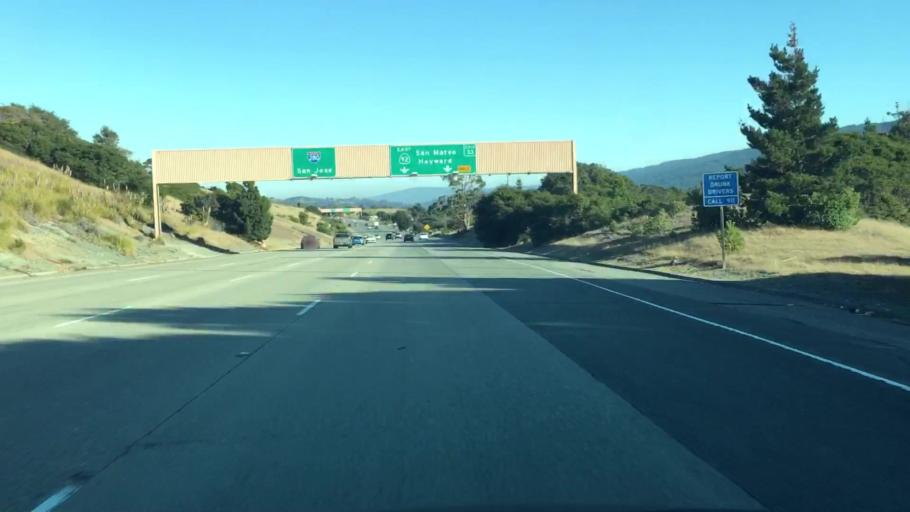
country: US
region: California
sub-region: San Mateo County
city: Highlands-Baywood Park
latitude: 37.5147
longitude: -122.3497
